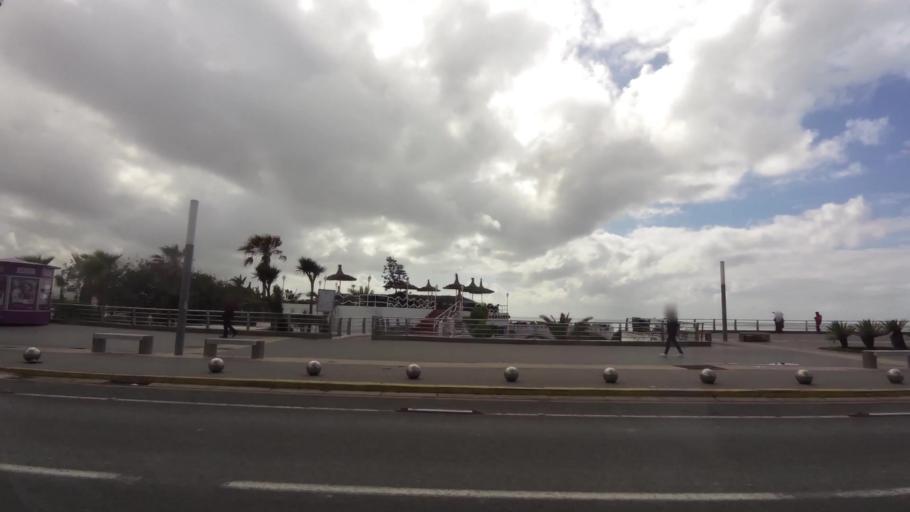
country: MA
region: Grand Casablanca
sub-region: Casablanca
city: Casablanca
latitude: 33.5938
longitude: -7.6786
